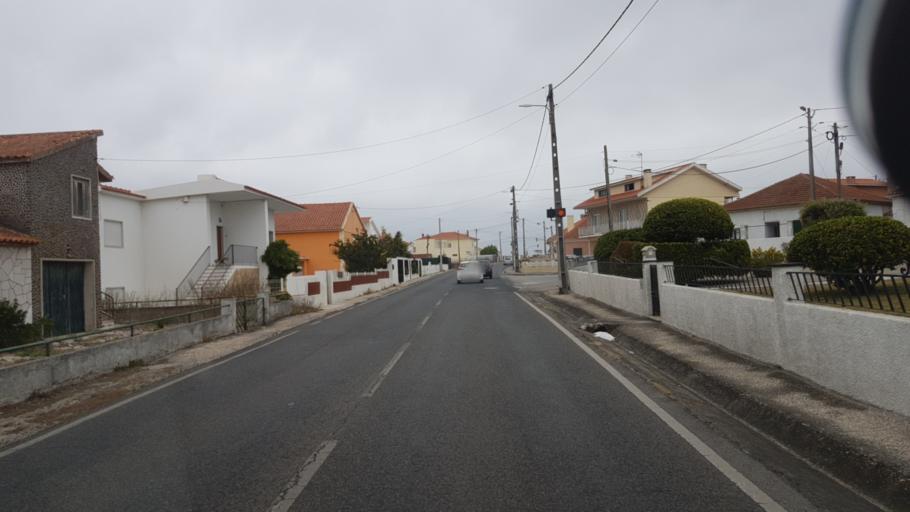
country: PT
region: Lisbon
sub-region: Torres Vedras
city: Silveira
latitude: 39.1210
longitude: -9.3765
